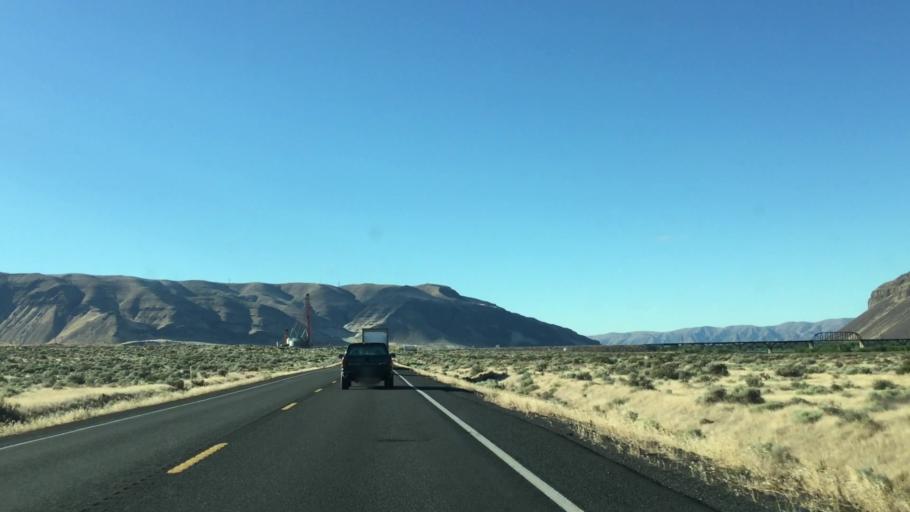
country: US
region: Washington
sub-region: Grant County
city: Mattawa
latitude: 46.8482
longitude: -119.9414
